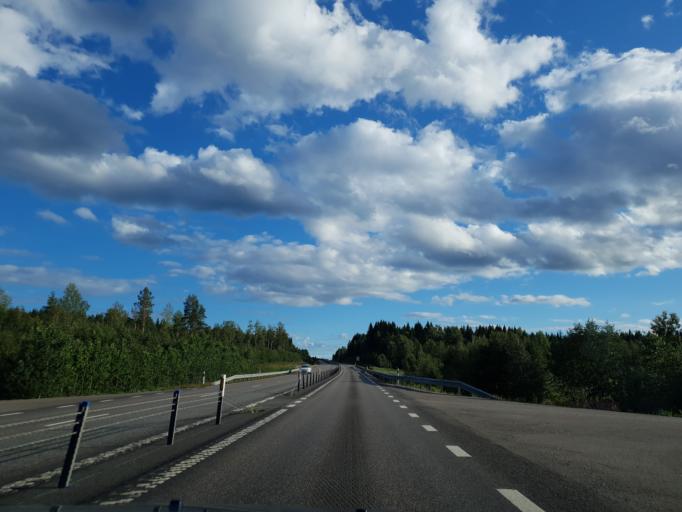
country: SE
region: Vaesternorrland
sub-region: Sundsvalls Kommun
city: Njurundabommen
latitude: 62.2233
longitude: 17.3716
